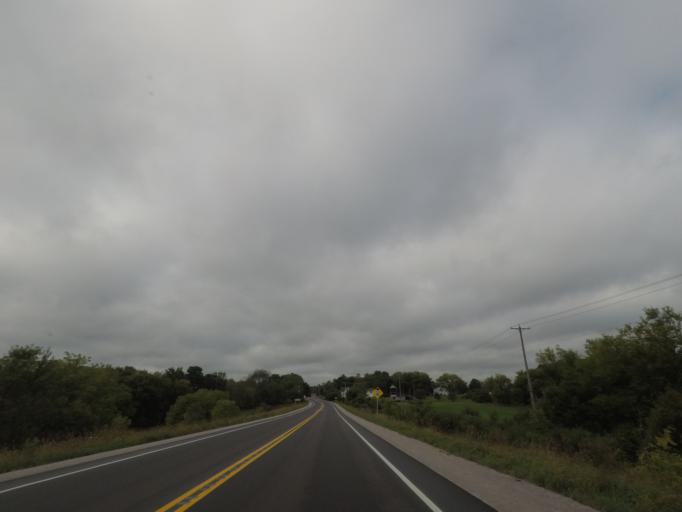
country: US
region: Wisconsin
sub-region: Jefferson County
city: Jefferson
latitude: 43.0095
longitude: -88.7683
